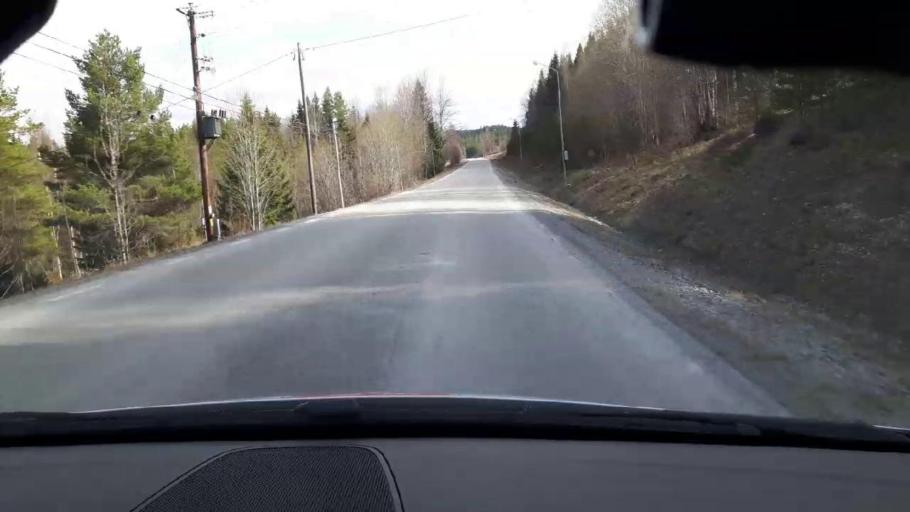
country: SE
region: Jaemtland
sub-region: Bergs Kommun
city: Hoverberg
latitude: 62.7283
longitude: 14.5991
